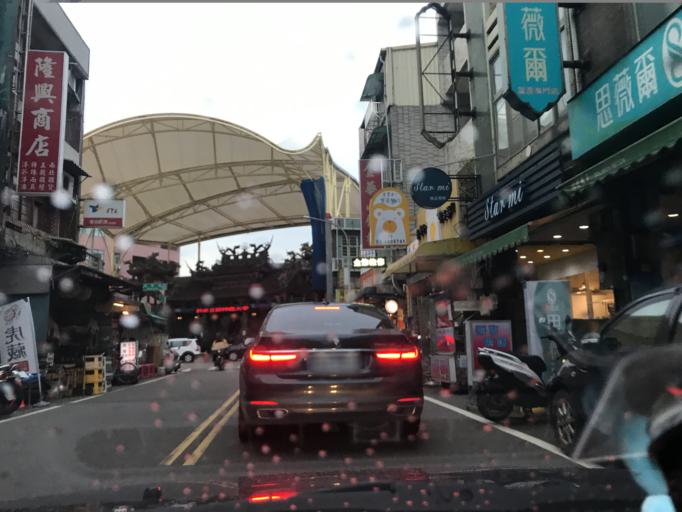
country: TW
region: Taiwan
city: Daxi
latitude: 24.8650
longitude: 121.2134
